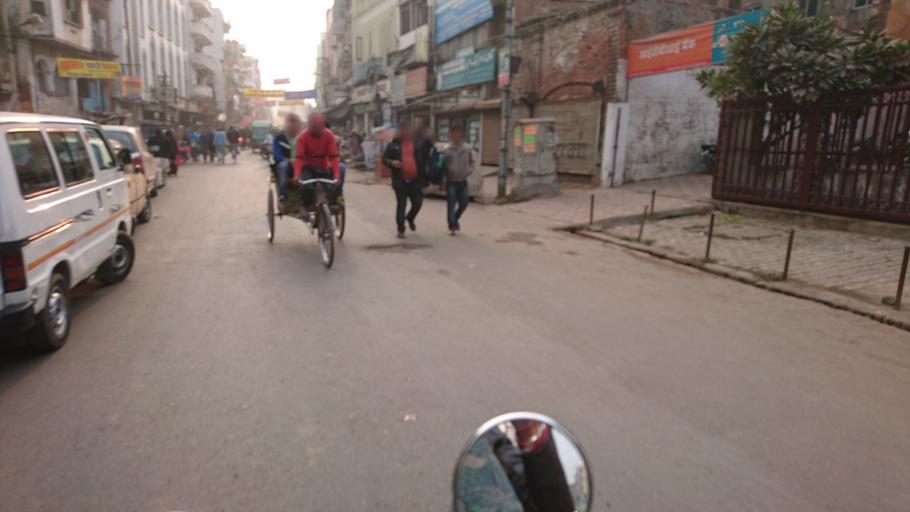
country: IN
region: Uttar Pradesh
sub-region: Lucknow District
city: Lucknow
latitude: 26.8512
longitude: 80.9266
